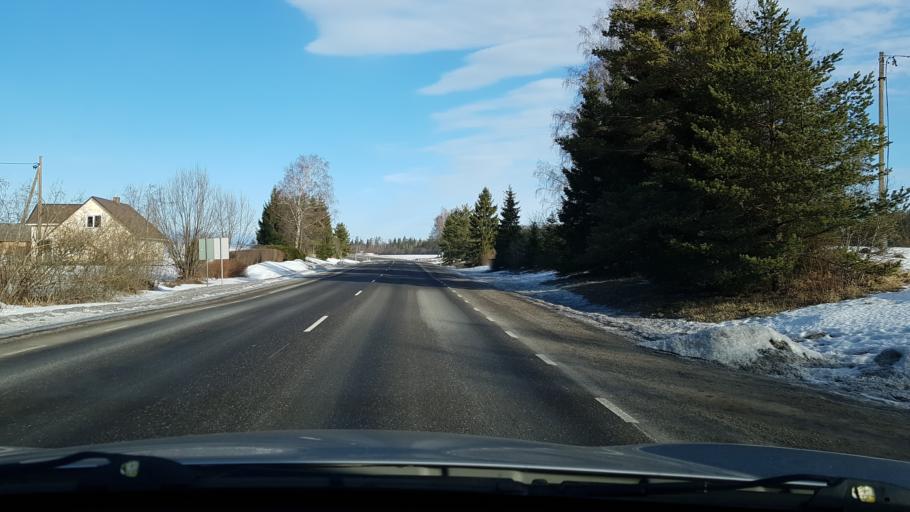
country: EE
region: Viljandimaa
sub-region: Viljandi linn
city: Viljandi
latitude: 58.4199
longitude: 25.5976
